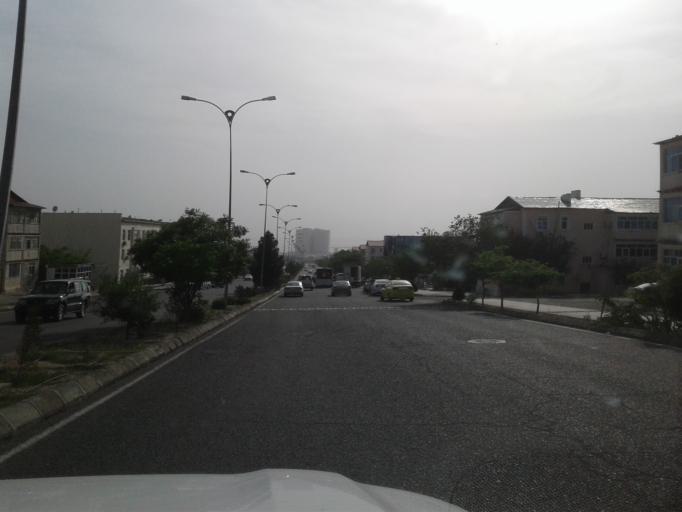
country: TM
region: Balkan
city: Turkmenbasy
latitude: 40.0011
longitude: 52.9767
